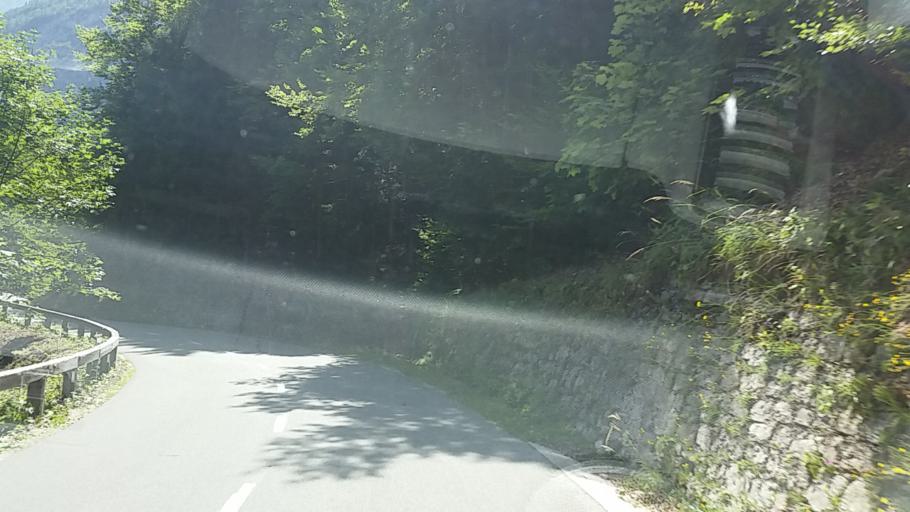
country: SI
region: Kranjska Gora
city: Kranjska Gora
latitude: 46.4480
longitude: 13.7756
